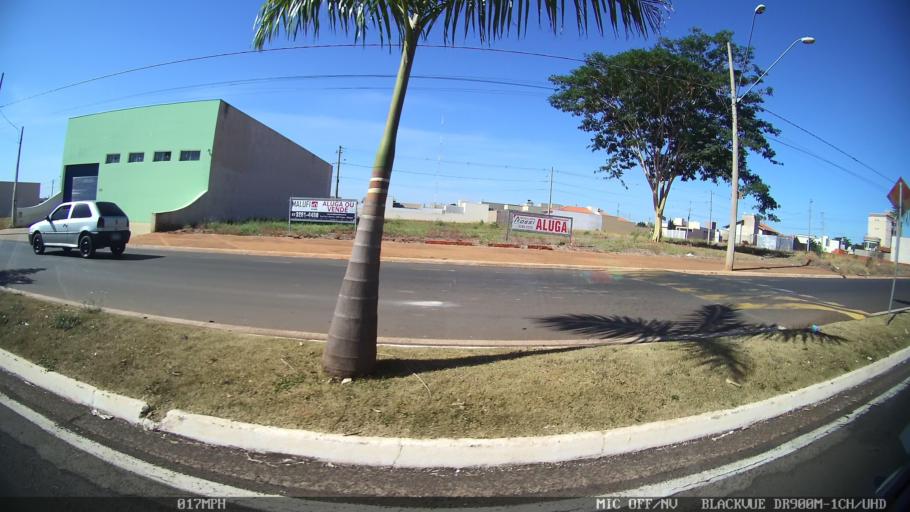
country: BR
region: Sao Paulo
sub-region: Olimpia
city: Olimpia
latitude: -20.7514
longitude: -48.9129
